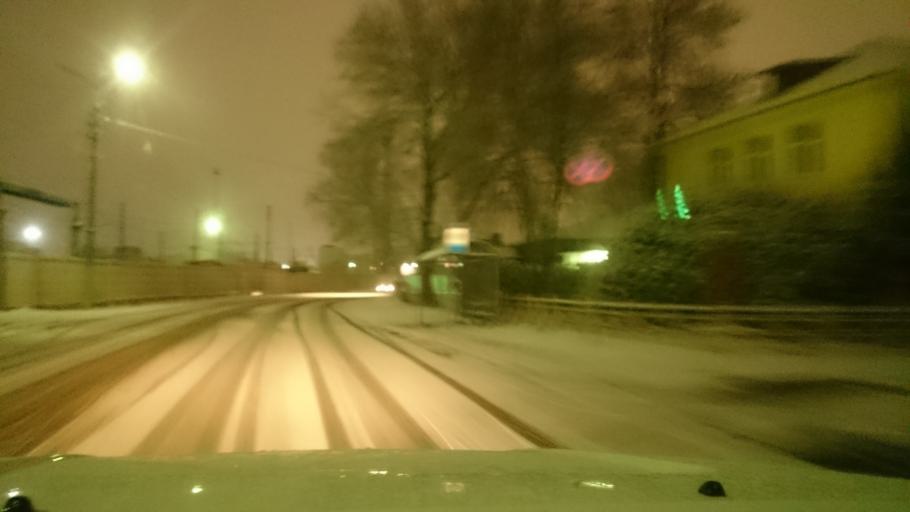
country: RU
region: Tula
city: Tula
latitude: 54.1934
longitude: 37.5741
